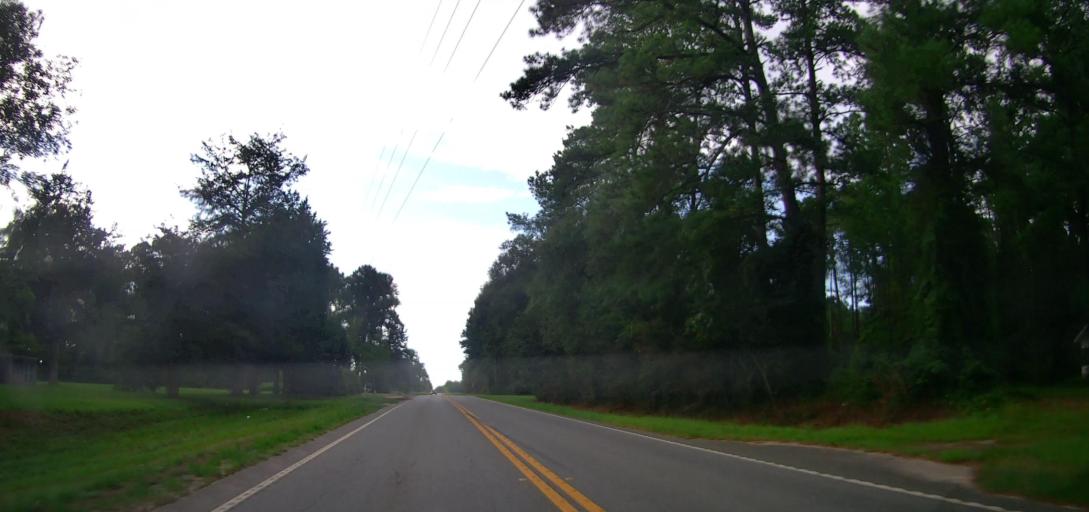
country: US
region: Georgia
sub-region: Ware County
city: Deenwood
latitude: 31.3127
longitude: -82.5687
